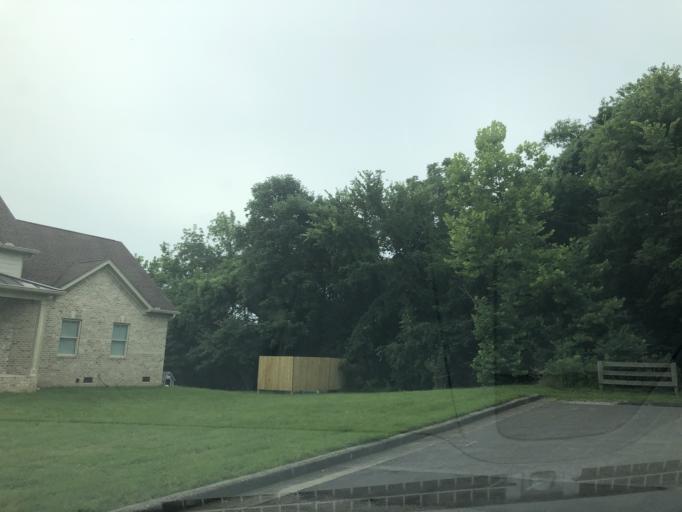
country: US
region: Tennessee
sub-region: Williamson County
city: Nolensville
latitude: 36.0176
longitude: -86.6893
